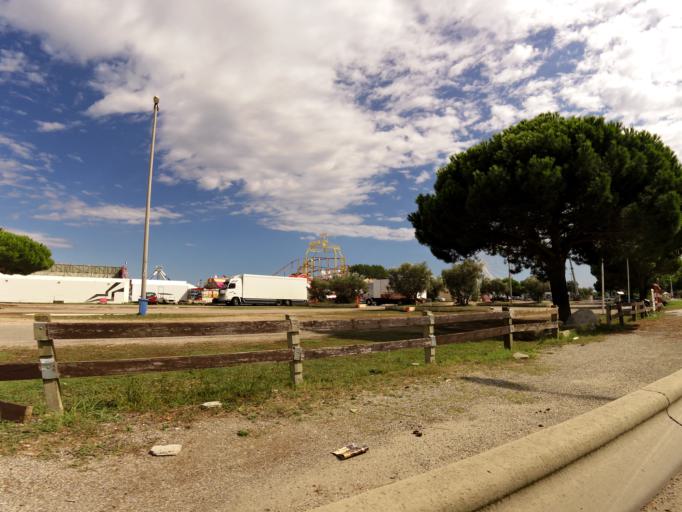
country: FR
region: Languedoc-Roussillon
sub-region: Departement du Gard
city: Le Grau-du-Roi
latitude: 43.5241
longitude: 4.1497
